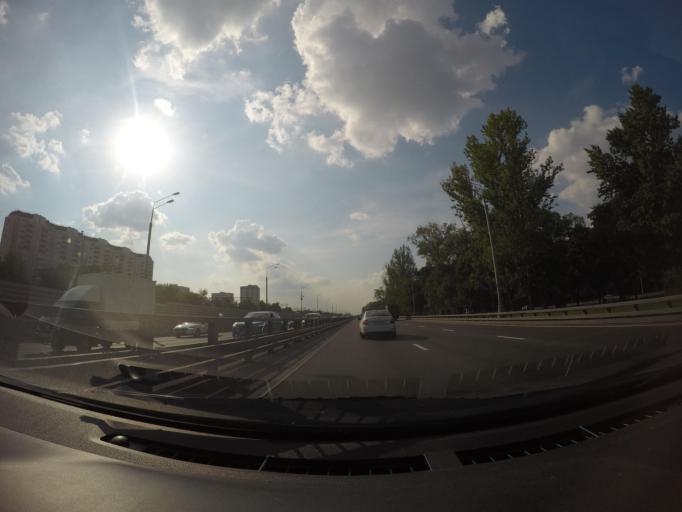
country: RU
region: Moscow
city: Veshnyaki
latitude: 55.7190
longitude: 37.8093
